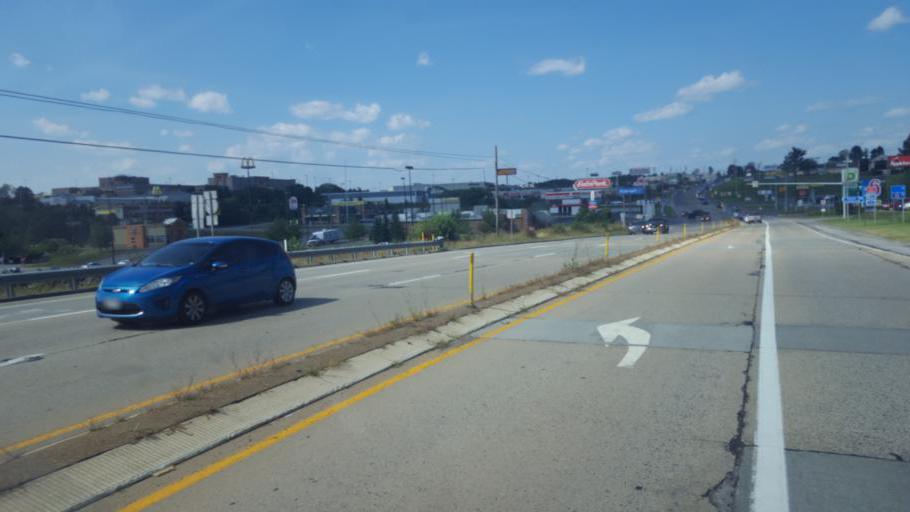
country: US
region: Pennsylvania
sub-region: Clarion County
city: Clarion
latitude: 41.1882
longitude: -79.3937
